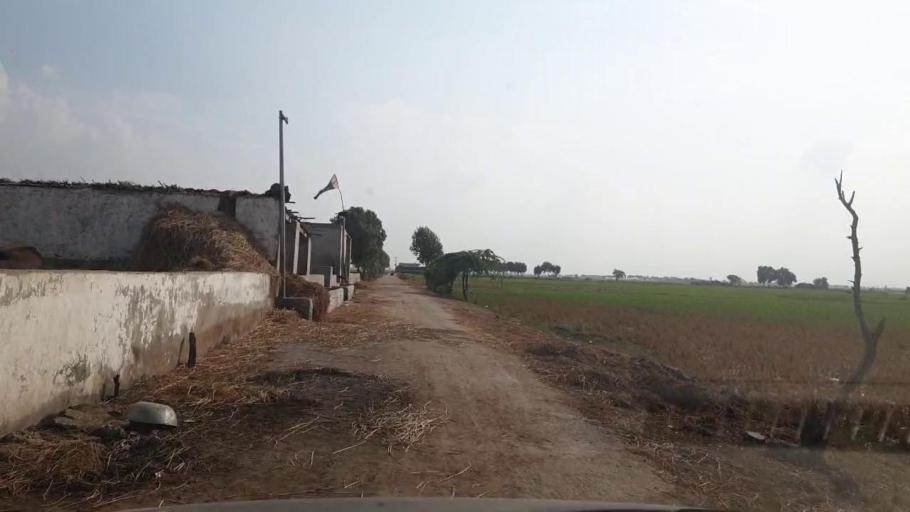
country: PK
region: Sindh
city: Kario
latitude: 24.6374
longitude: 68.5580
